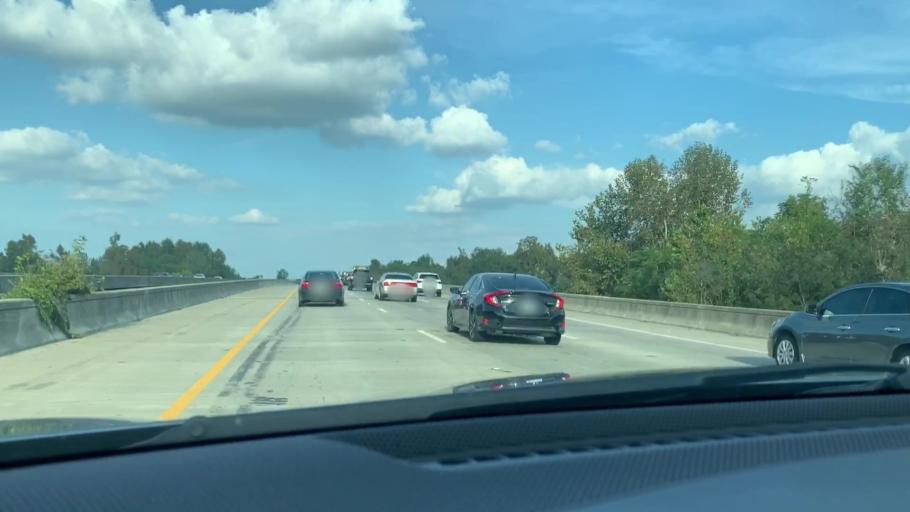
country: US
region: South Carolina
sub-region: Lexington County
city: Cayce
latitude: 33.9315
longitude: -81.0190
